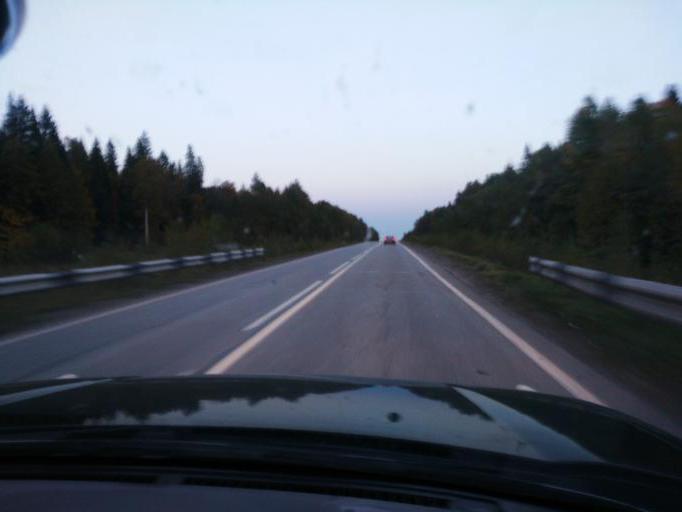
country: RU
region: Perm
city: Verkhnechusovskiye Gorodki
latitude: 58.2631
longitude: 56.9704
